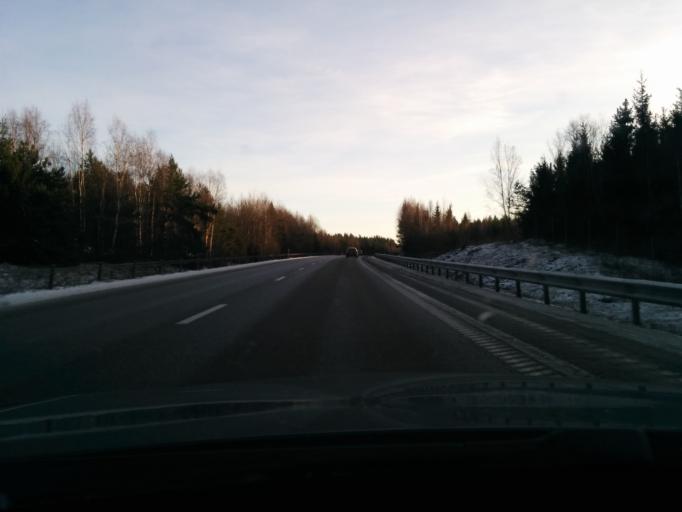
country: SE
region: Stockholm
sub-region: Upplands-Bro Kommun
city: Bro
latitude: 59.5538
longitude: 17.5868
